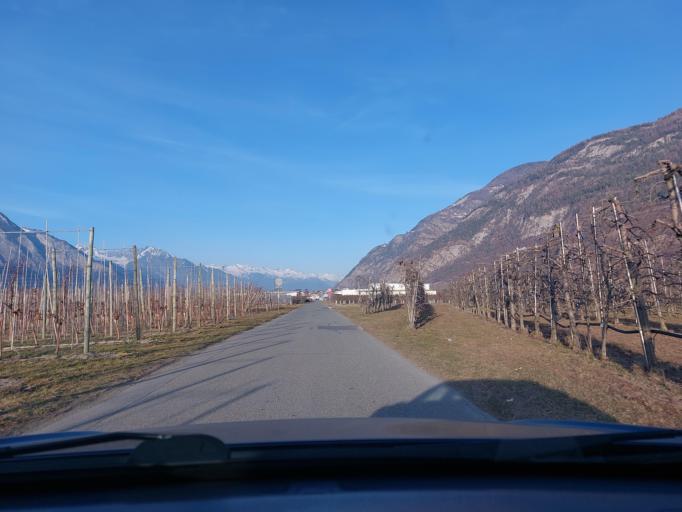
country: CH
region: Valais
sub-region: Martigny District
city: Saxon
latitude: 46.1570
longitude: 7.1932
